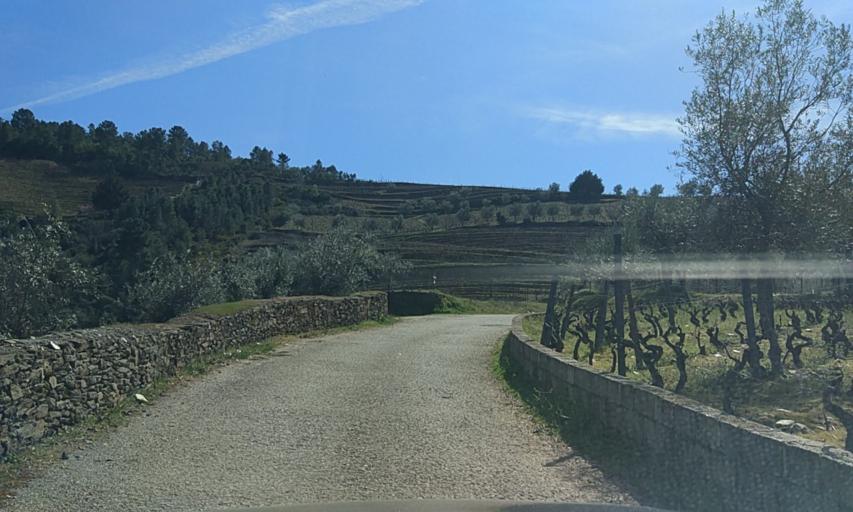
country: PT
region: Vila Real
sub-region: Sabrosa
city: Sabrosa
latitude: 41.3057
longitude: -7.5463
